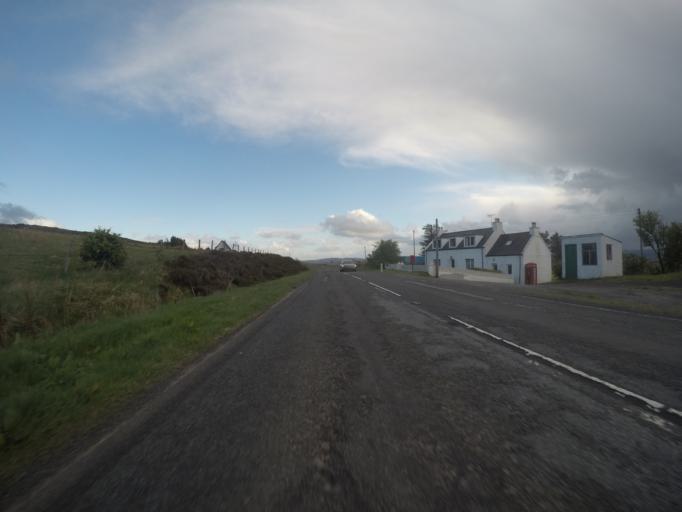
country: GB
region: Scotland
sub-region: Highland
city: Portree
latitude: 57.5667
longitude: -6.3647
